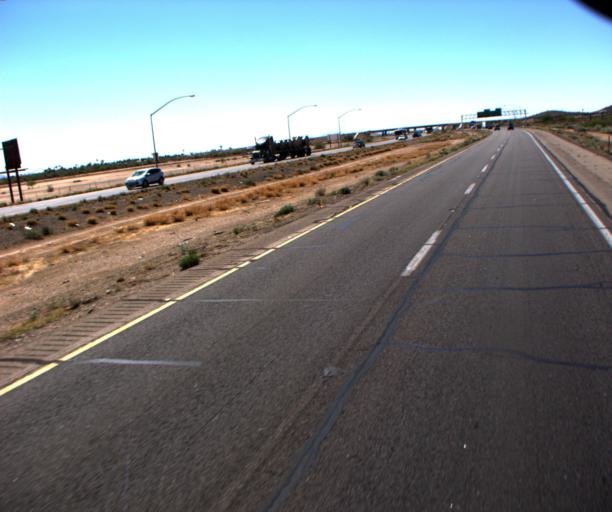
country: US
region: Arizona
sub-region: Pinal County
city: Arizona City
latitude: 32.8257
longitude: -111.6853
